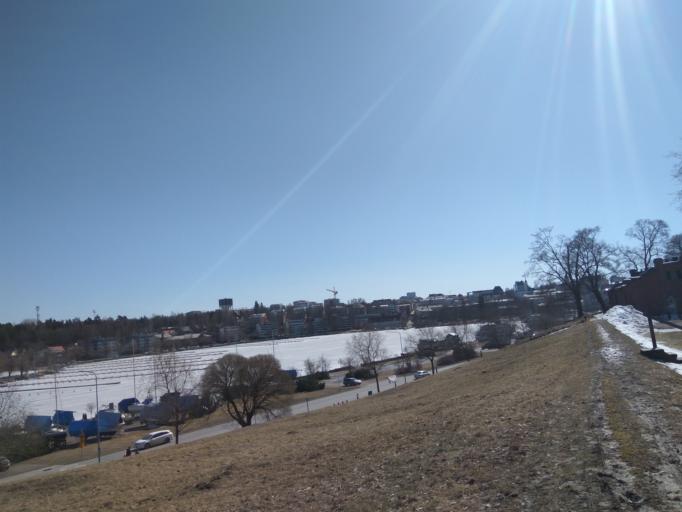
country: FI
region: South Karelia
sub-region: Lappeenranta
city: Lappeenranta
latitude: 61.0668
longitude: 28.1854
